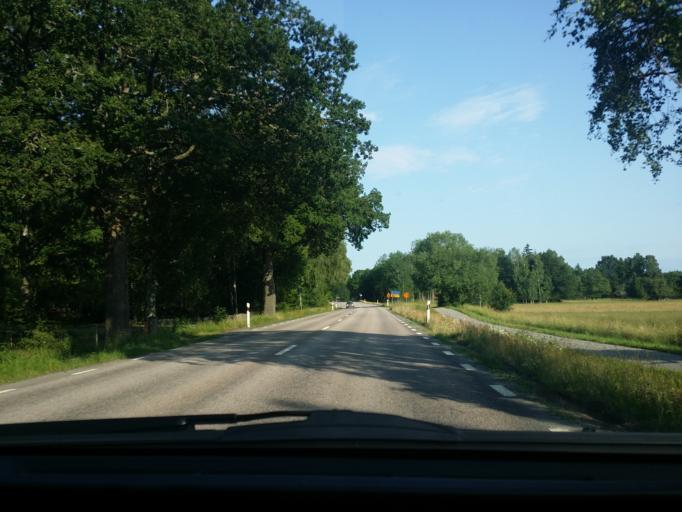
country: SE
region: Vaestmanland
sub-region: Vasteras
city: Tillberga
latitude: 59.6027
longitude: 16.6575
